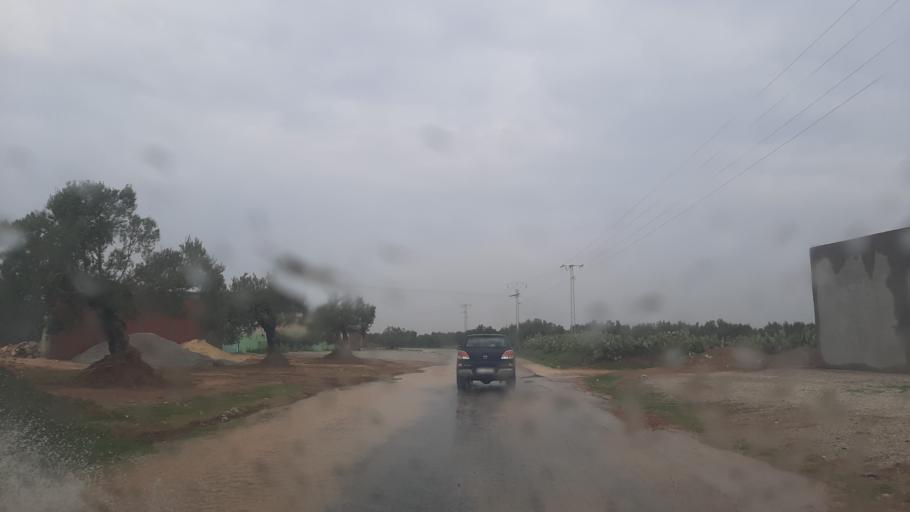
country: TN
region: Al Munastir
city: Sidi Bin Nur
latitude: 35.4730
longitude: 10.8811
